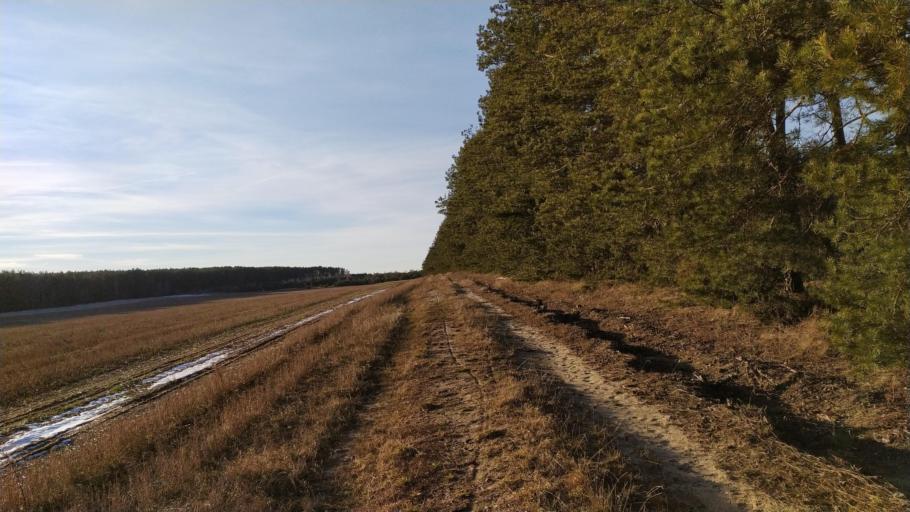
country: BY
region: Brest
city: Kamyanyets
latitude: 52.3701
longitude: 23.8566
